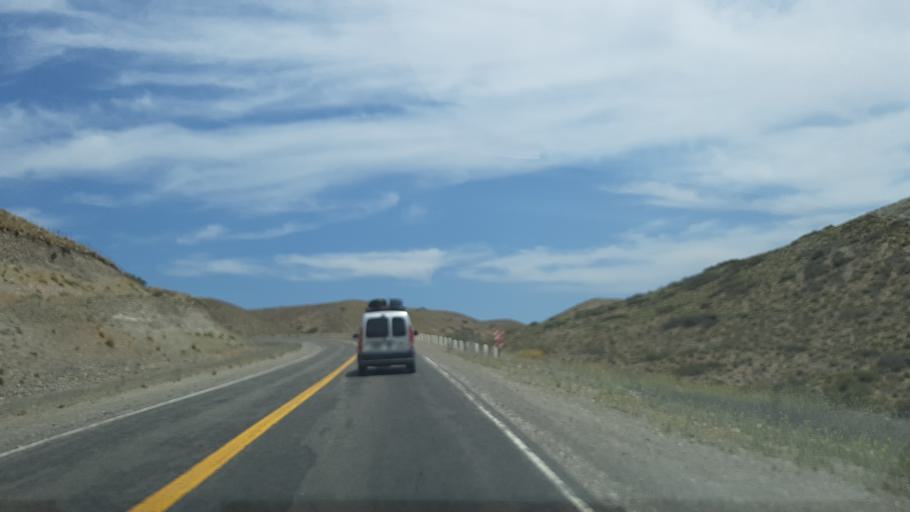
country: AR
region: Rio Negro
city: Pilcaniyeu
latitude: -40.4831
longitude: -70.6767
